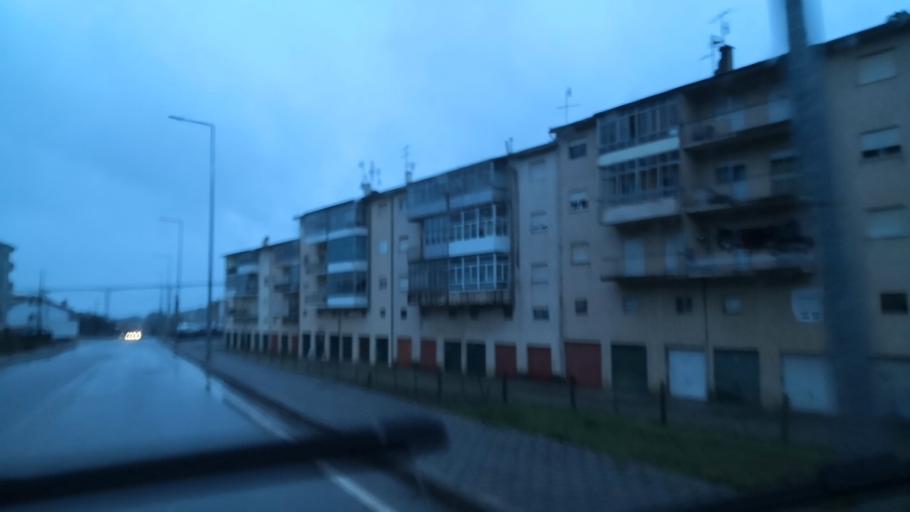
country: PT
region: Vila Real
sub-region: Vila Pouca de Aguiar
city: Vila Pouca de Aguiar
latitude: 41.4961
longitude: -7.6427
